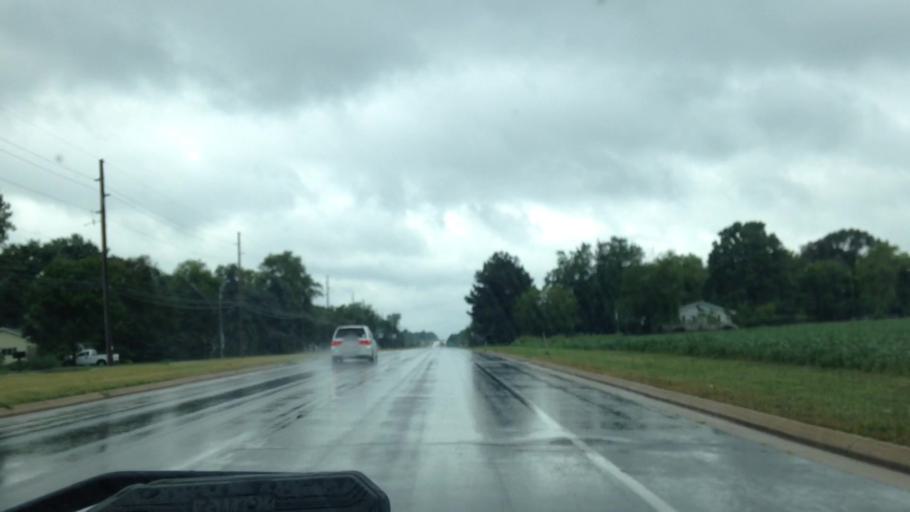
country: US
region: Wisconsin
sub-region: Waukesha County
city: Menomonee Falls
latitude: 43.1923
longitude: -88.1540
